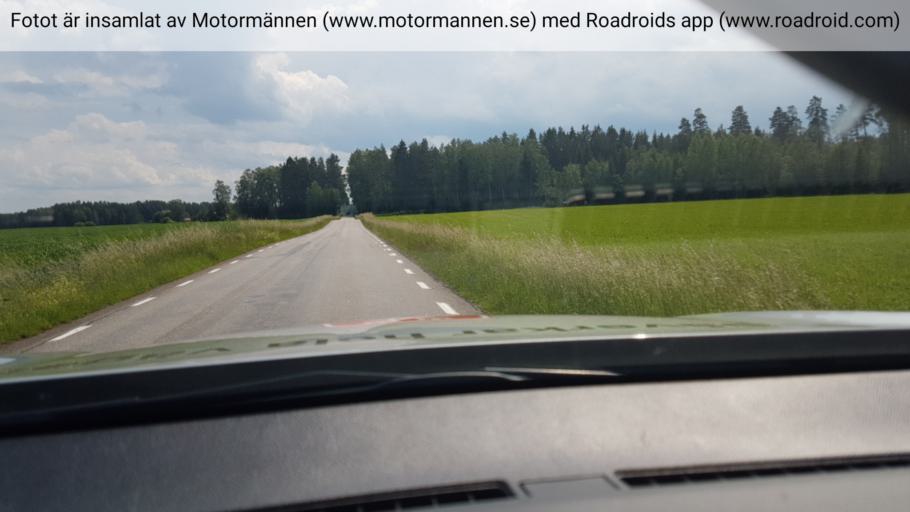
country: SE
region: Vaestra Goetaland
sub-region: Skara Kommun
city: Skara
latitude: 58.4453
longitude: 13.3953
